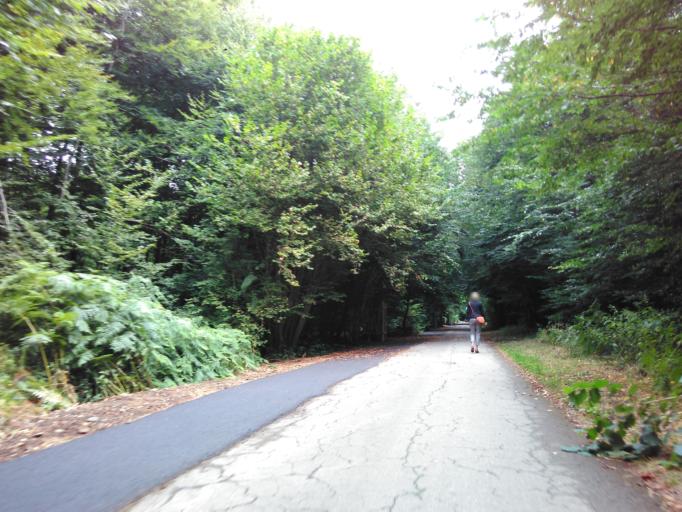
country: LU
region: Luxembourg
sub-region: Canton de Luxembourg
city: Sandweiler
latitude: 49.6440
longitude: 6.2100
